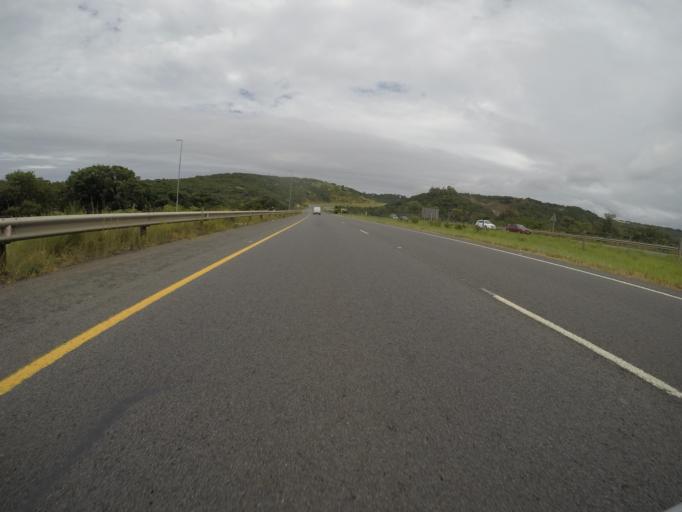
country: ZA
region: Eastern Cape
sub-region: Buffalo City Metropolitan Municipality
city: East London
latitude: -32.9643
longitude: 27.9195
